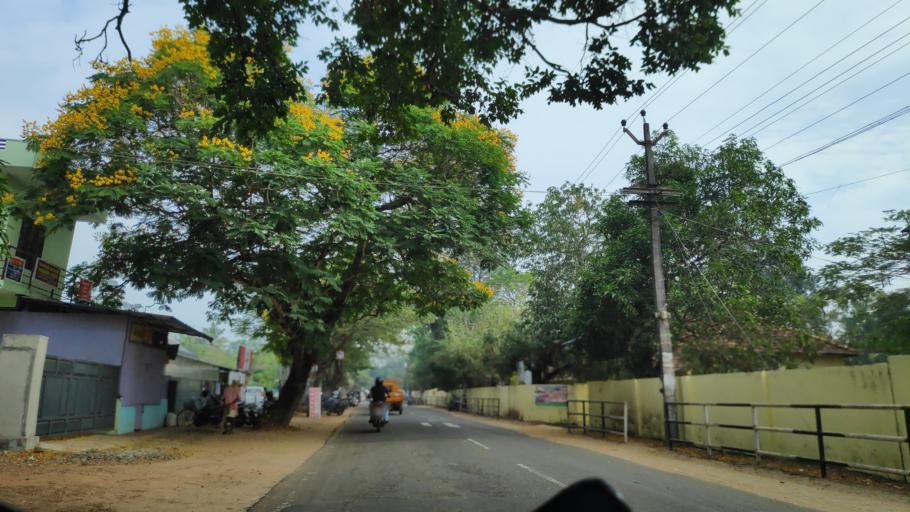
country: IN
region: Kerala
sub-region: Alappuzha
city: Vayalar
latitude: 9.7178
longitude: 76.3599
